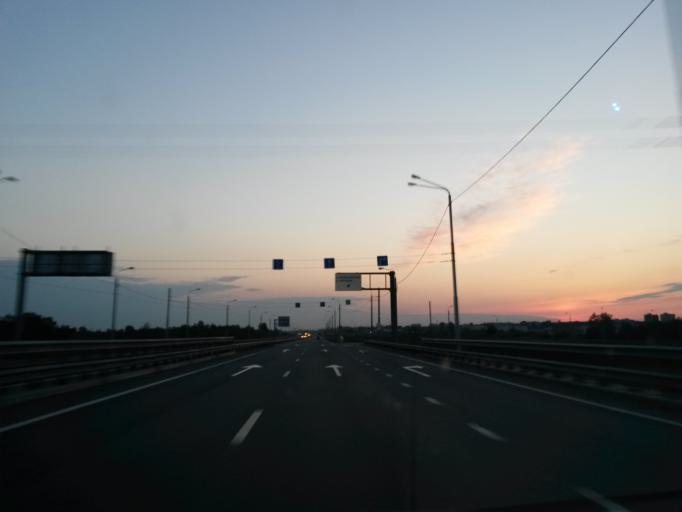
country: RU
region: Jaroslavl
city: Yaroslavl
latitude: 57.6676
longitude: 39.8176
